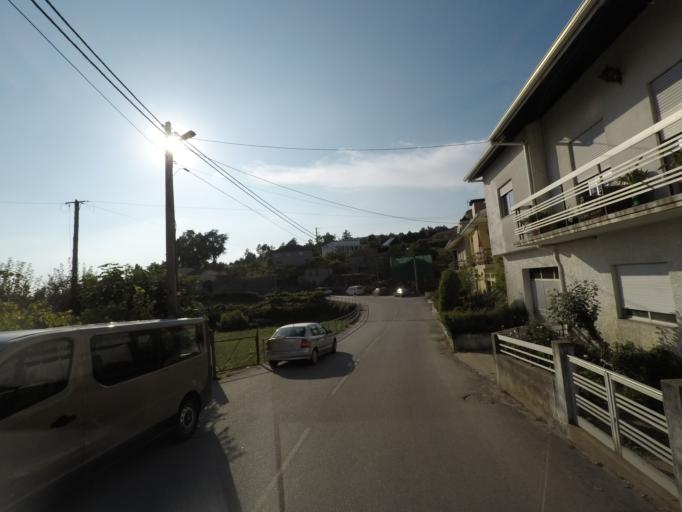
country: PT
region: Porto
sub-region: Baiao
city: Valadares
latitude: 41.1667
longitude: -7.9297
